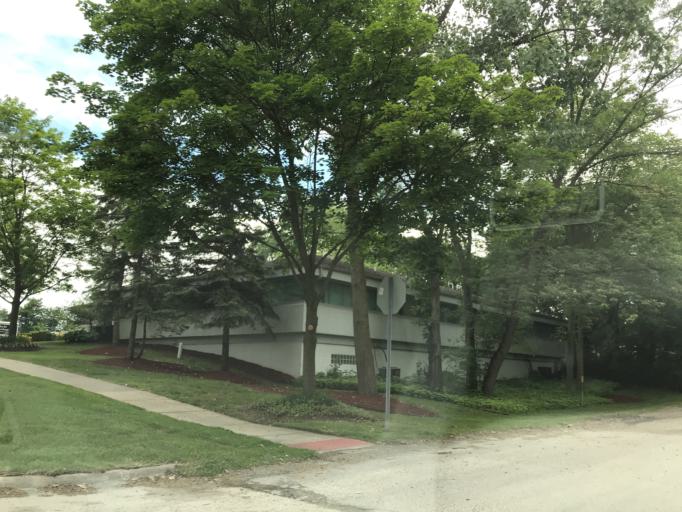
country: US
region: Michigan
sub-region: Oakland County
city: Farmington
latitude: 42.4460
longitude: -83.3366
